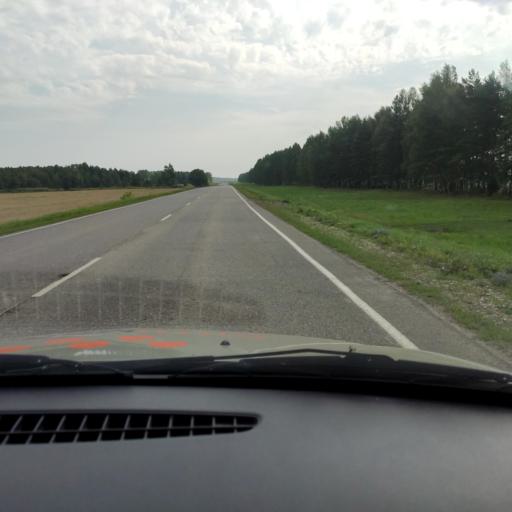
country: RU
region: Bashkortostan
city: Krasnaya Gorka
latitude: 55.0552
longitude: 56.5422
